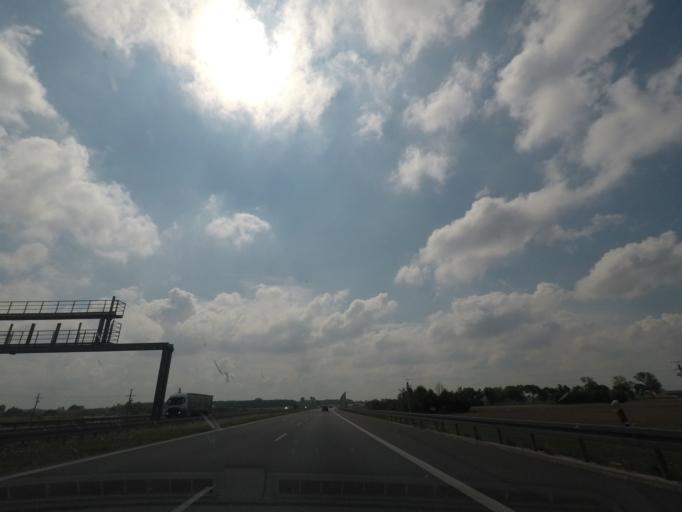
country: PL
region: Lodz Voivodeship
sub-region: Powiat kutnowski
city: Krzyzanow
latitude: 52.2070
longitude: 19.4824
